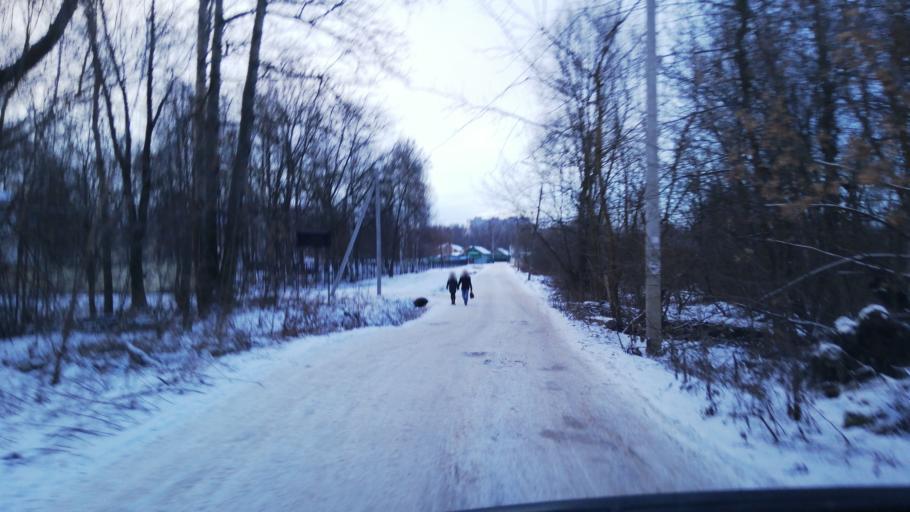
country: RU
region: Jaroslavl
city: Yaroslavl
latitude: 57.5979
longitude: 39.8422
